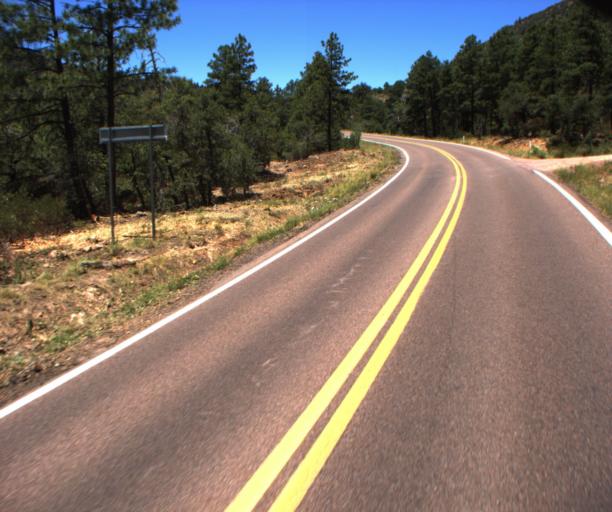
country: US
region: Arizona
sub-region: Gila County
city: Pine
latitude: 34.3980
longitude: -111.4692
